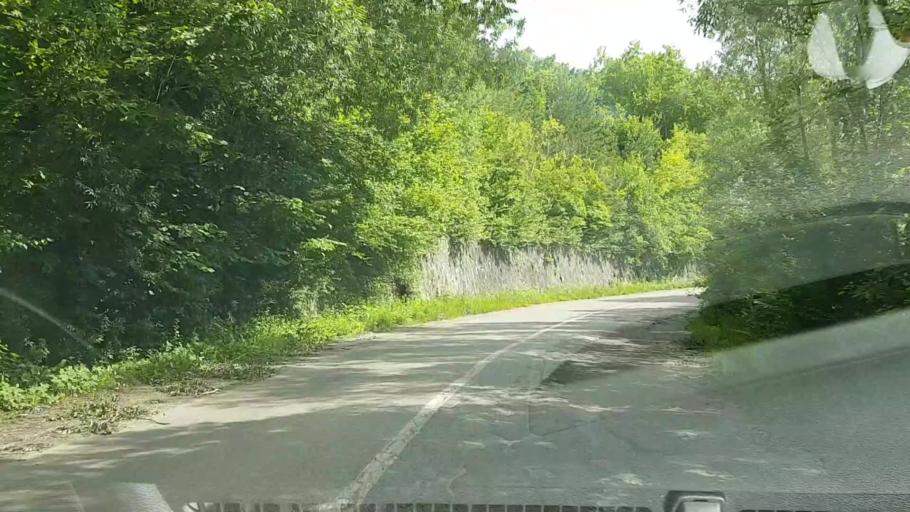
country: RO
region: Neamt
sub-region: Comuna Hangu
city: Hangu
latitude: 47.0279
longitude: 26.0683
